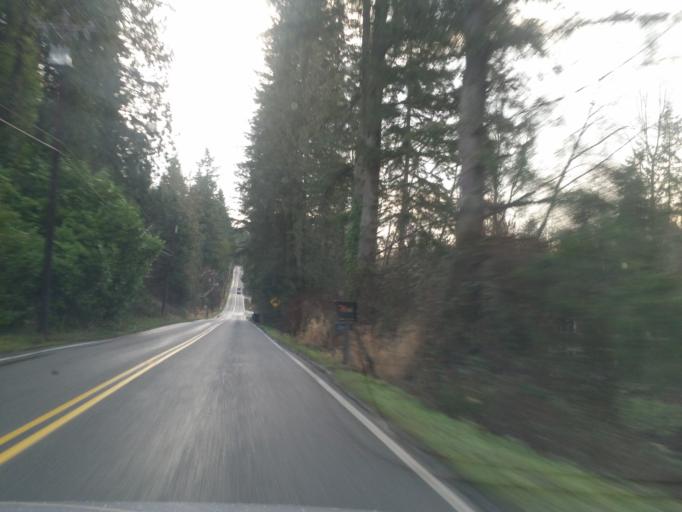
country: US
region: Washington
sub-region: Snohomish County
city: Cathcart
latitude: 47.8231
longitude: -122.0935
